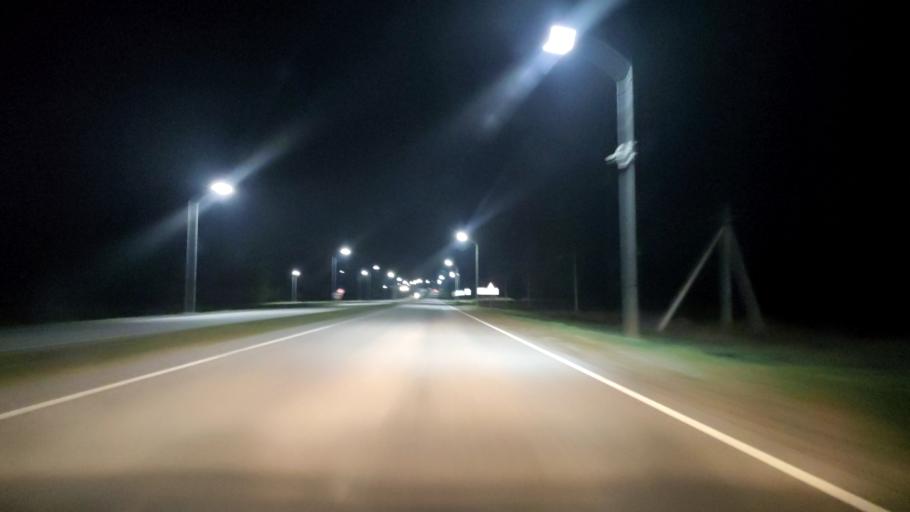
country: RU
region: Belgorod
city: Staryy Oskol
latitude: 51.3883
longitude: 37.8634
